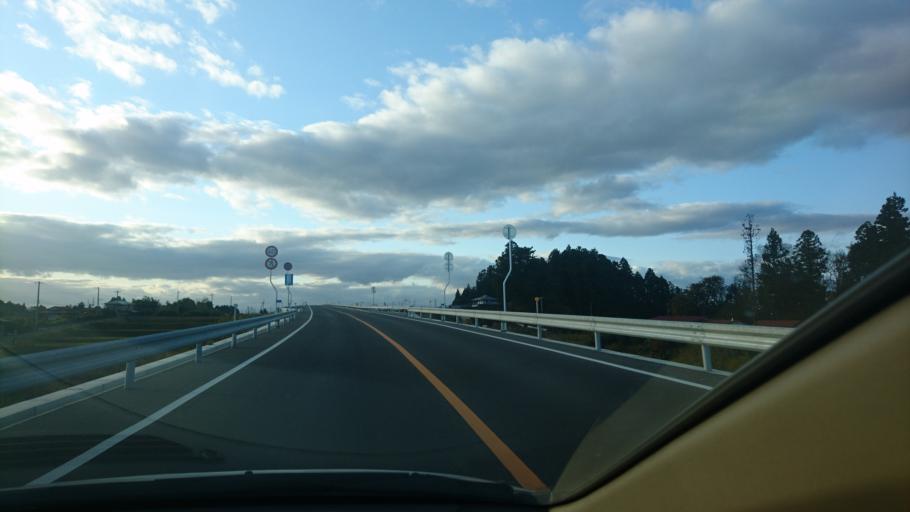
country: JP
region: Miyagi
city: Kogota
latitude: 38.7365
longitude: 141.0500
